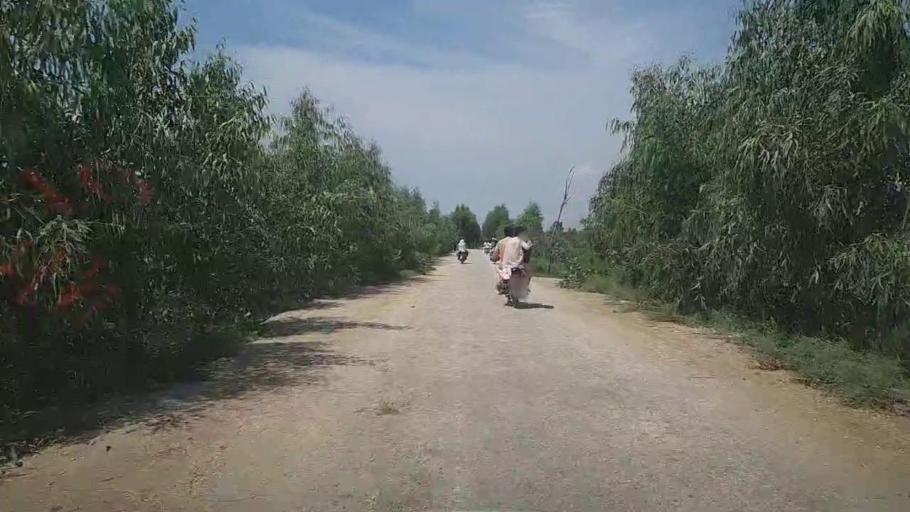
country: PK
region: Sindh
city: Kandhkot
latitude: 28.2944
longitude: 69.2373
